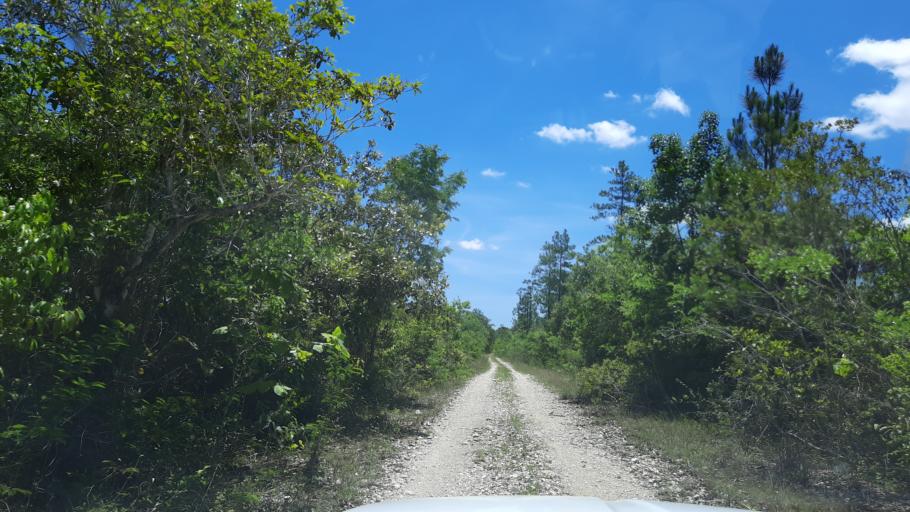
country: BZ
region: Cayo
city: Belmopan
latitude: 17.3598
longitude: -88.5326
